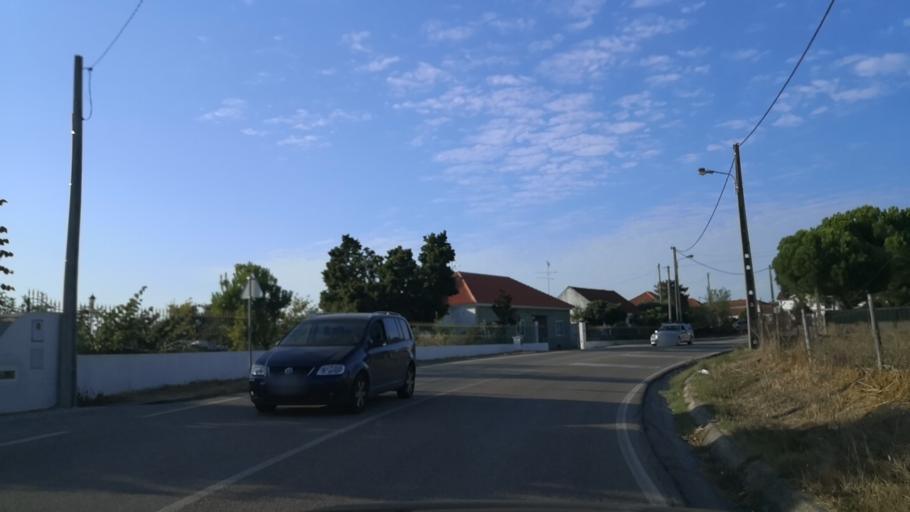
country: PT
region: Santarem
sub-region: Santarem
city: Santarem
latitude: 39.3370
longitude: -8.6638
